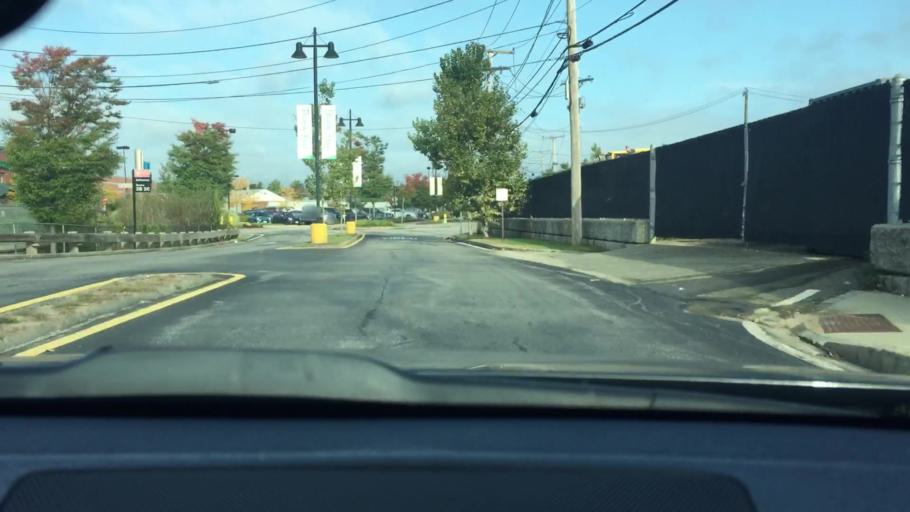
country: US
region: Massachusetts
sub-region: Norfolk County
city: Dedham
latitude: 42.2320
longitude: -71.1761
